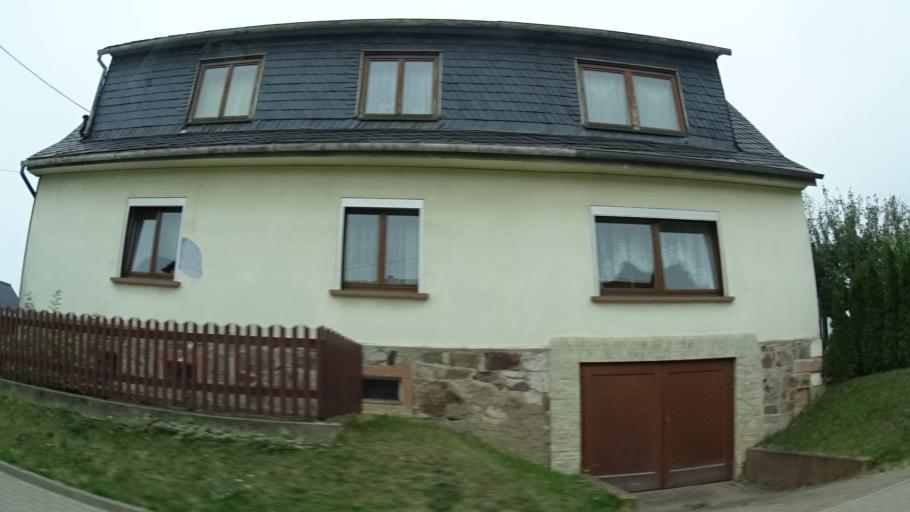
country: DE
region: Thuringia
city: Pennewitz
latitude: 50.6562
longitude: 11.0504
